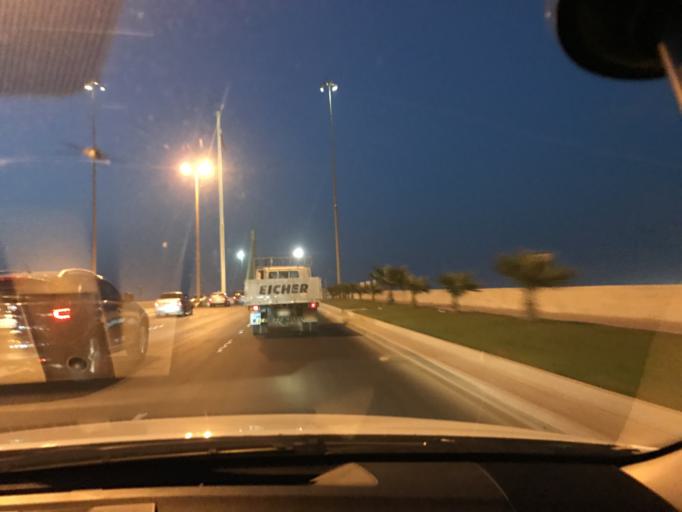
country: BH
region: Muharraq
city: Al Muharraq
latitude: 26.2512
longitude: 50.5929
